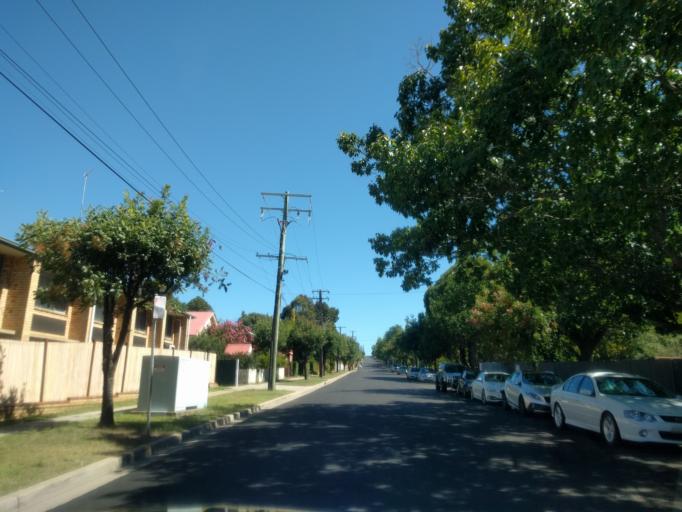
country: AU
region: New South Wales
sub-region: Armidale Dumaresq
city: Armidale
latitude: -30.5171
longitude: 151.6659
